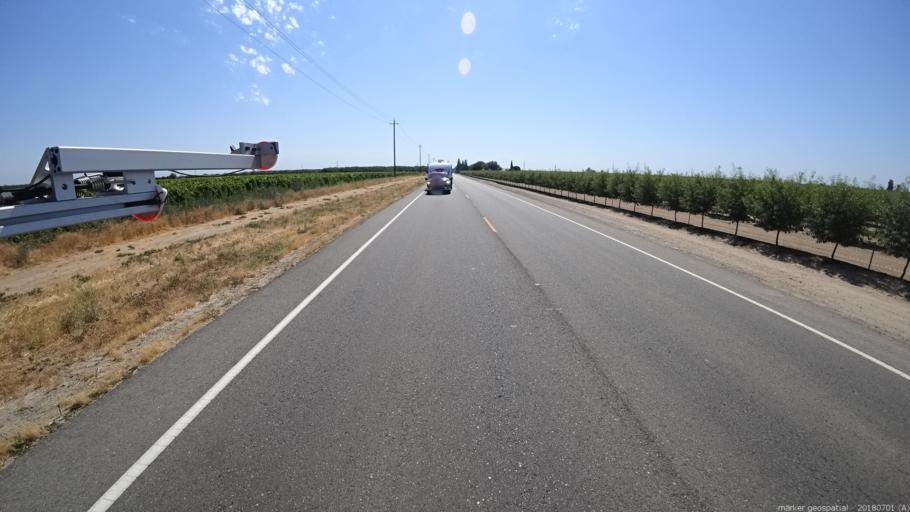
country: US
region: California
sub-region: Madera County
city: Parksdale
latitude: 36.8806
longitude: -119.9287
